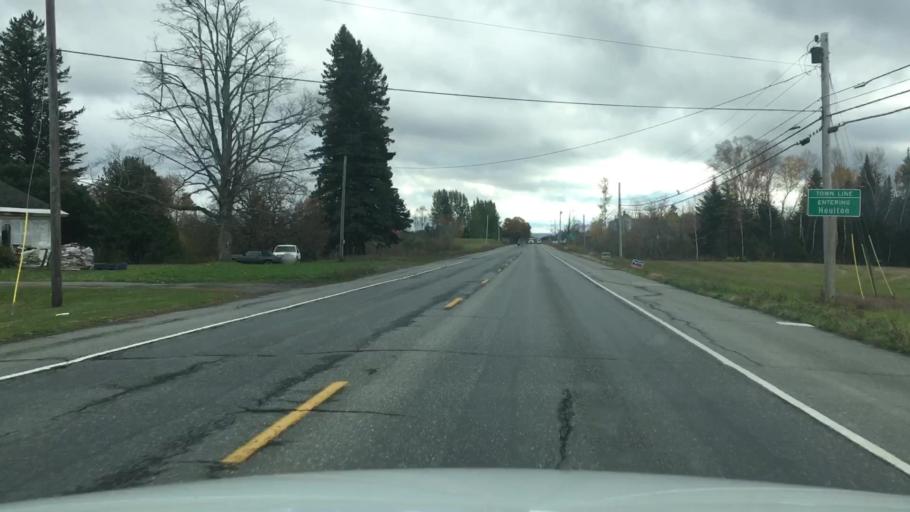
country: US
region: Maine
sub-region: Aroostook County
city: Houlton
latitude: 46.1855
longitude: -67.8412
